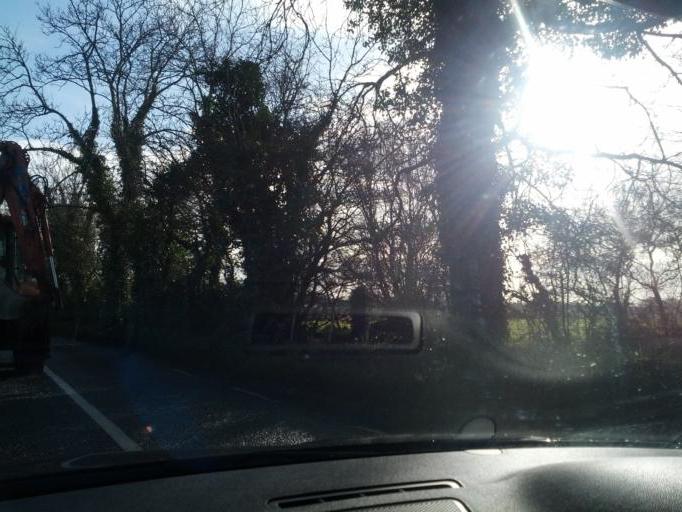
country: IE
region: Connaught
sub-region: County Galway
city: Athenry
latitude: 53.3882
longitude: -8.6669
